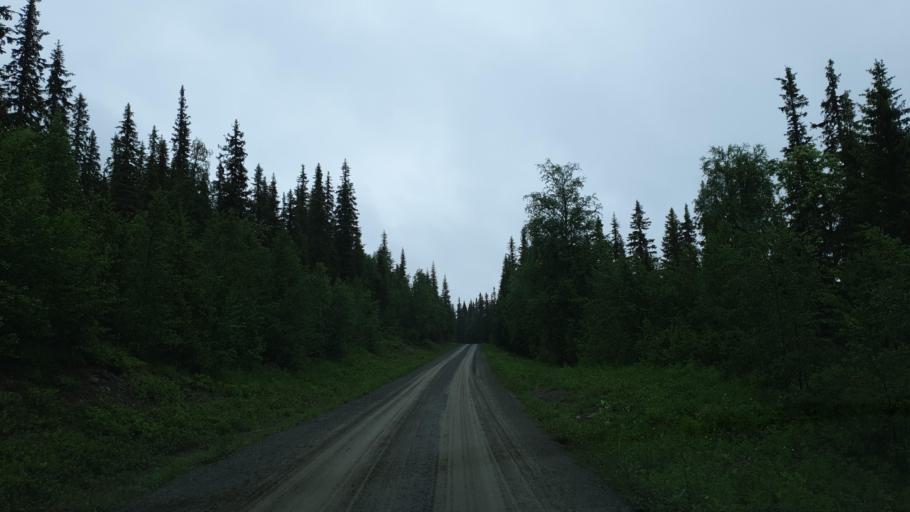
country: SE
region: Vaesterbotten
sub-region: Vilhelmina Kommun
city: Sjoberg
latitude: 65.3321
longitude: 15.9056
